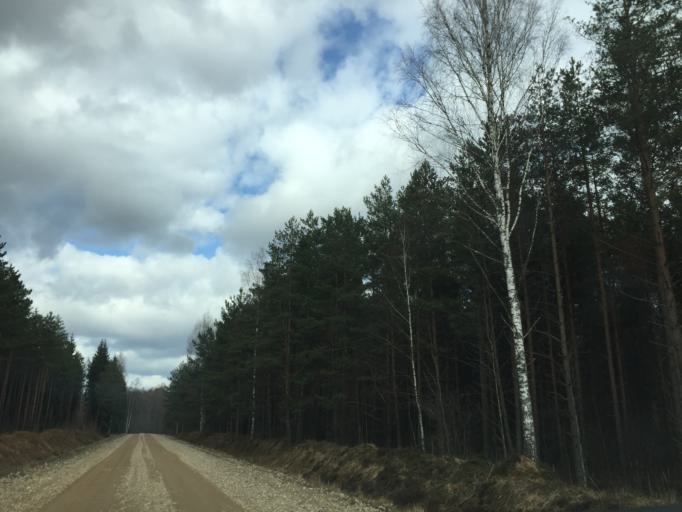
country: LV
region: Vecumnieki
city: Vecumnieki
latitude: 56.5973
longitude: 24.6397
